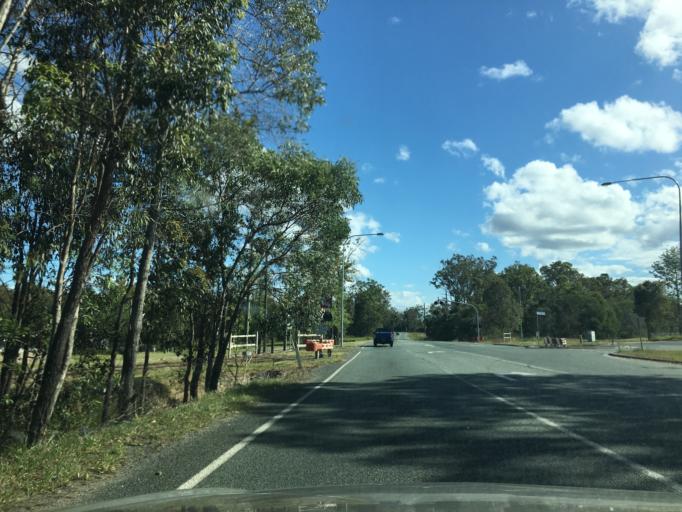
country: AU
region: Queensland
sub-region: Logan
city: Chambers Flat
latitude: -27.7781
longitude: 153.1016
